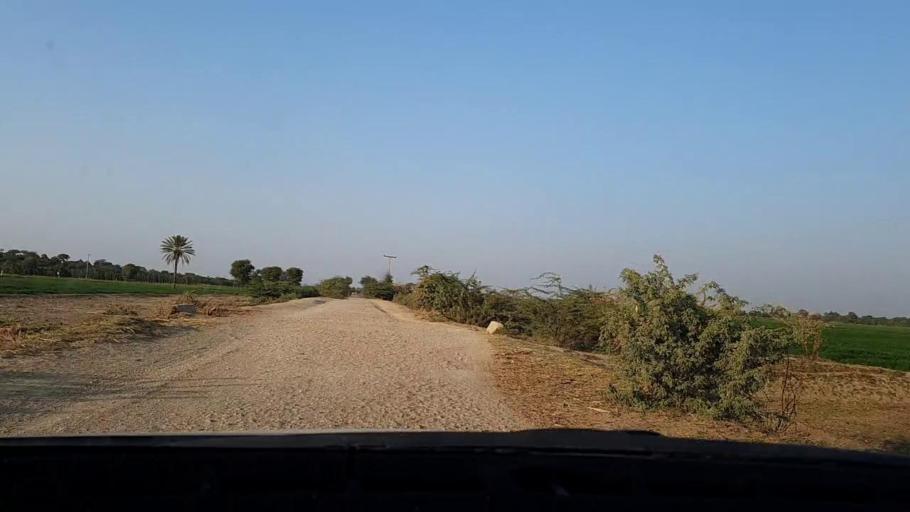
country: PK
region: Sindh
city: Tando Mittha Khan
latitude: 25.8588
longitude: 69.2725
